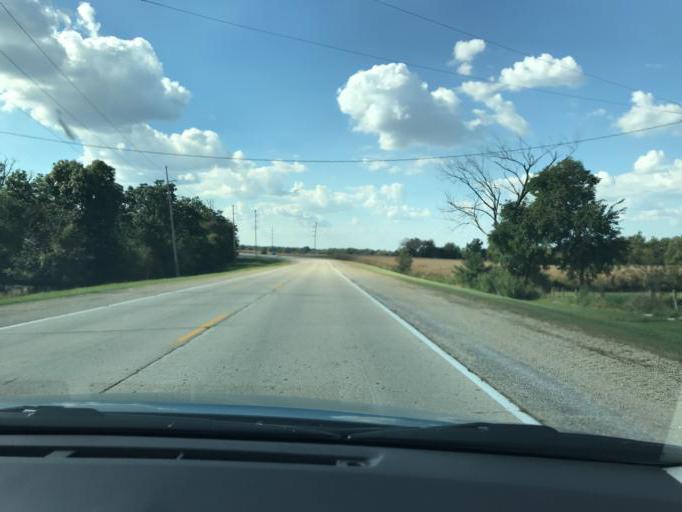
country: US
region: Wisconsin
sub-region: Rock County
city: Orfordville
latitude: 42.5549
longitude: -89.2840
